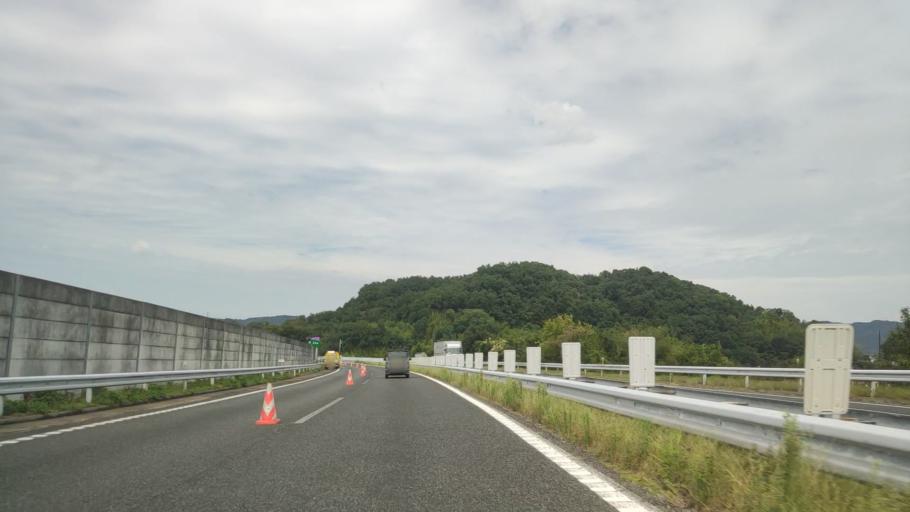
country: JP
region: Wakayama
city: Kainan
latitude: 34.1892
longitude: 135.2386
